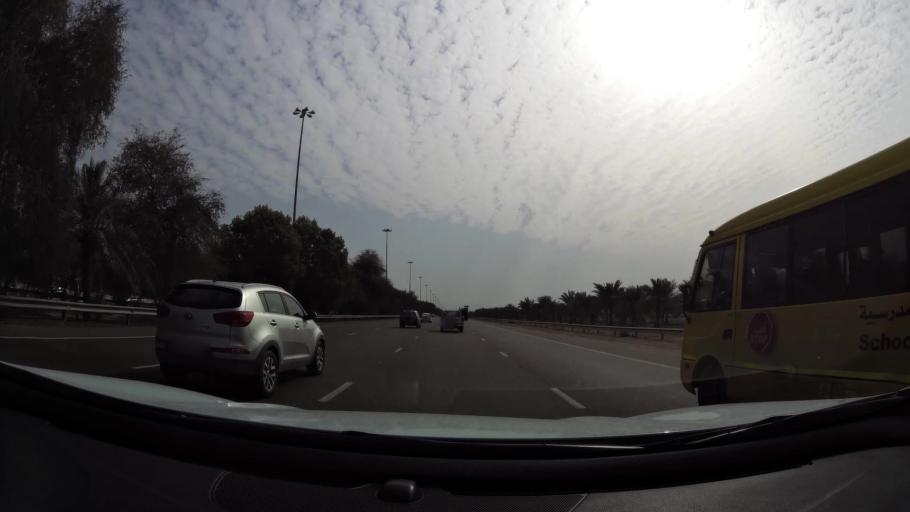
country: AE
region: Abu Dhabi
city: Abu Dhabi
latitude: 24.6112
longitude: 54.7124
